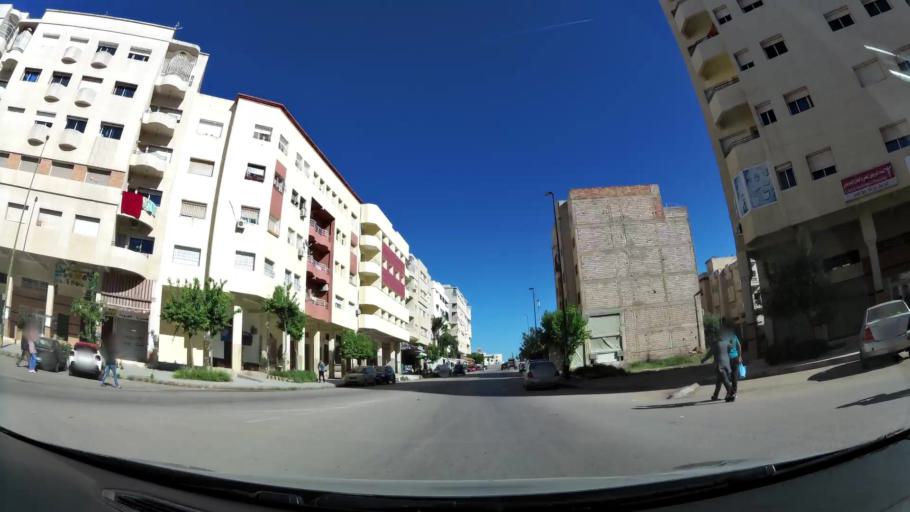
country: MA
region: Fes-Boulemane
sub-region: Fes
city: Fes
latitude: 34.0093
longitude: -4.9652
